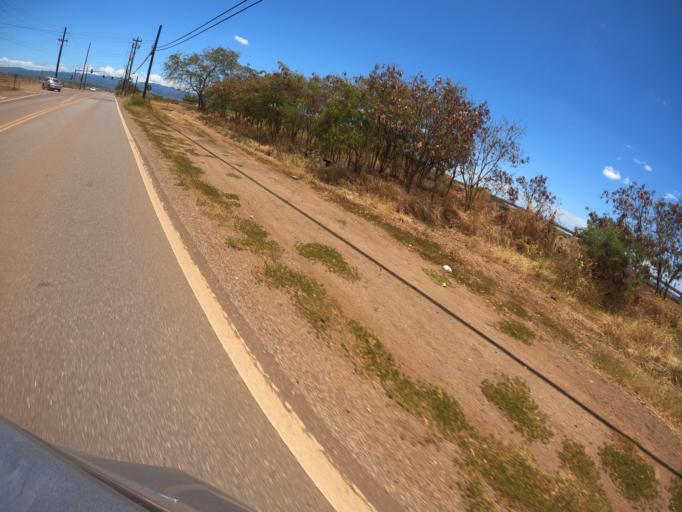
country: US
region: Hawaii
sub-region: Honolulu County
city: Royal Kunia
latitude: 21.3718
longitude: -158.0448
